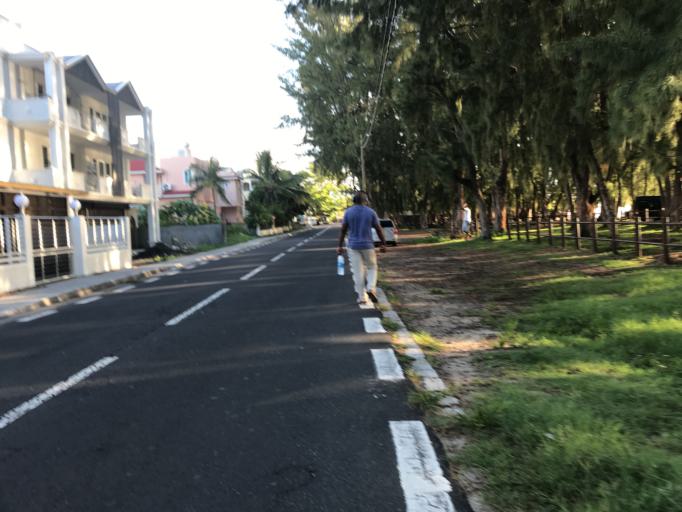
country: MU
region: Black River
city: Flic en Flac
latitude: -20.2918
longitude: 57.3638
